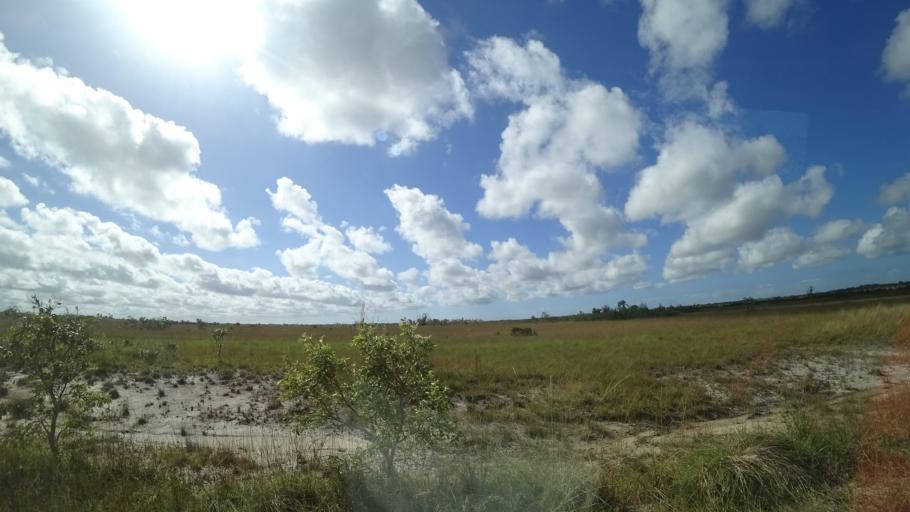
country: MZ
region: Sofala
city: Beira
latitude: -19.6253
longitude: 35.0604
